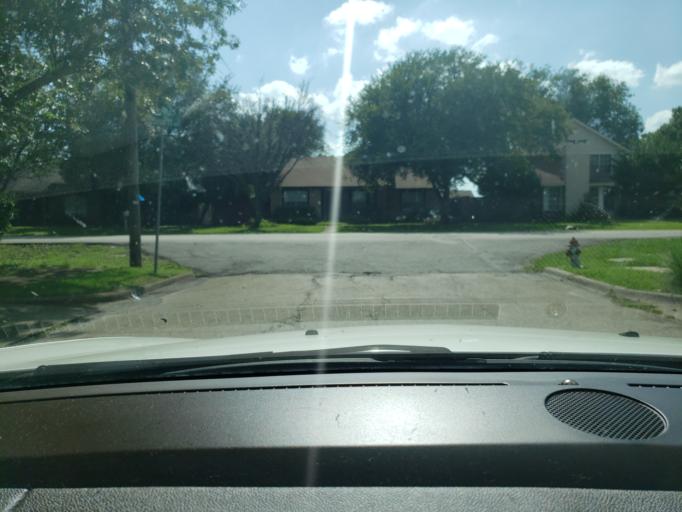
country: US
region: Texas
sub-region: Dallas County
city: Rowlett
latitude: 32.8946
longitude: -96.5739
